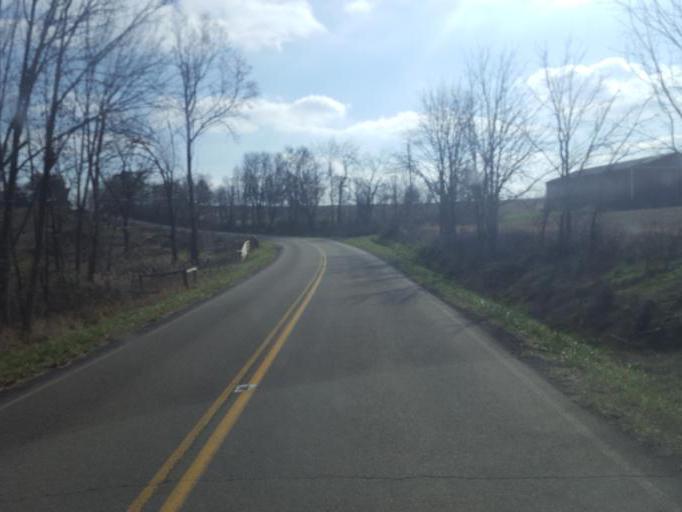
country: US
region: Ohio
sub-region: Knox County
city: Oak Hill
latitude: 40.4293
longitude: -82.1414
